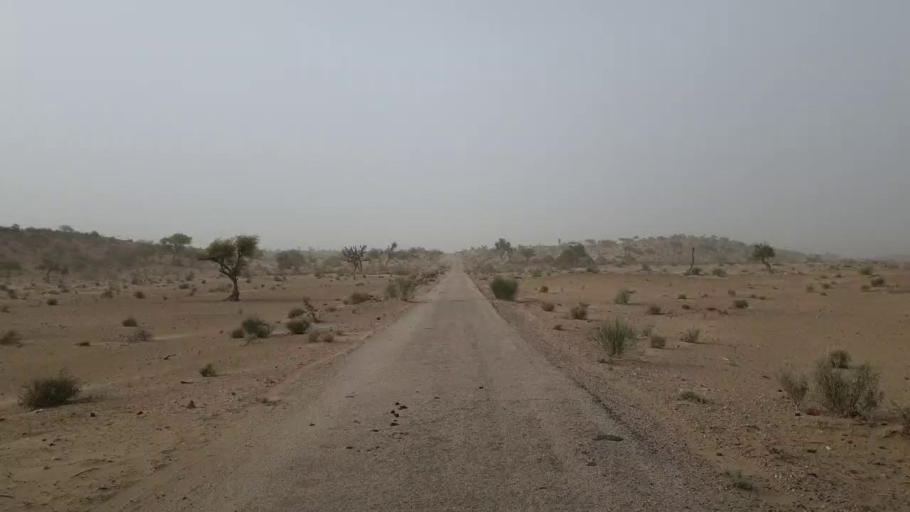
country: PK
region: Sindh
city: Islamkot
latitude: 24.5547
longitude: 70.3610
